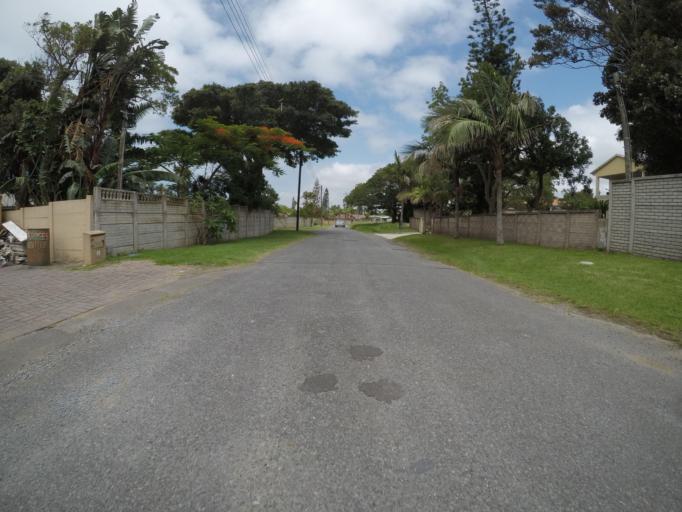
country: ZA
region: Eastern Cape
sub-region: Buffalo City Metropolitan Municipality
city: East London
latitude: -32.9449
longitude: 28.0049
